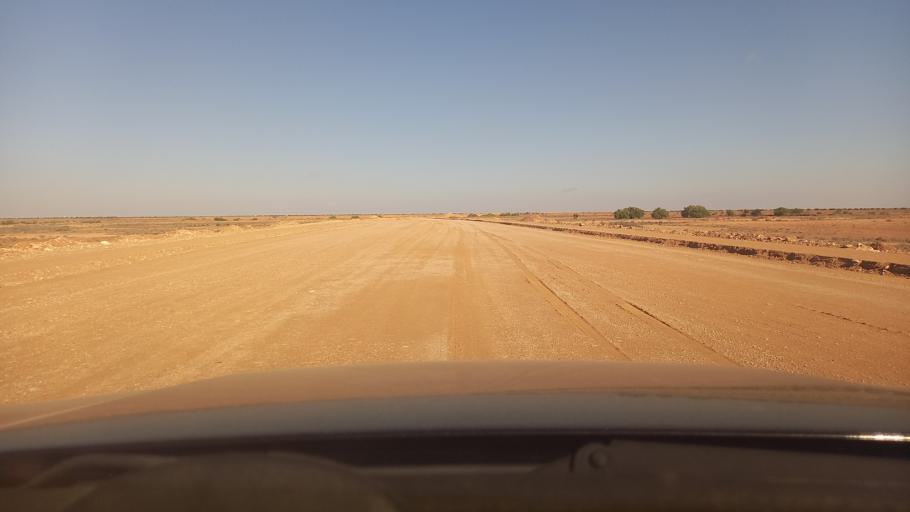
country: TN
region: Madanin
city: Medenine
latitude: 33.1400
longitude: 10.5055
